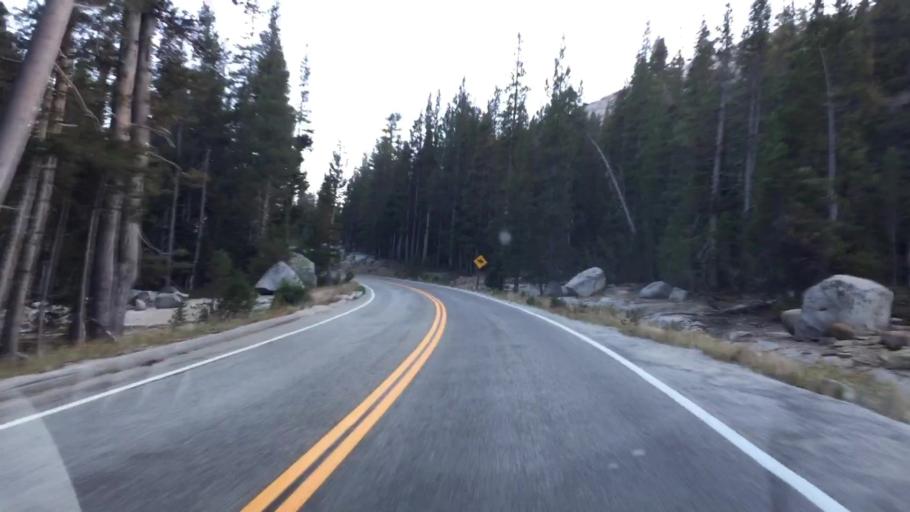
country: US
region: California
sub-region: Mariposa County
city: Yosemite Valley
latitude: 37.8233
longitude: -119.4775
